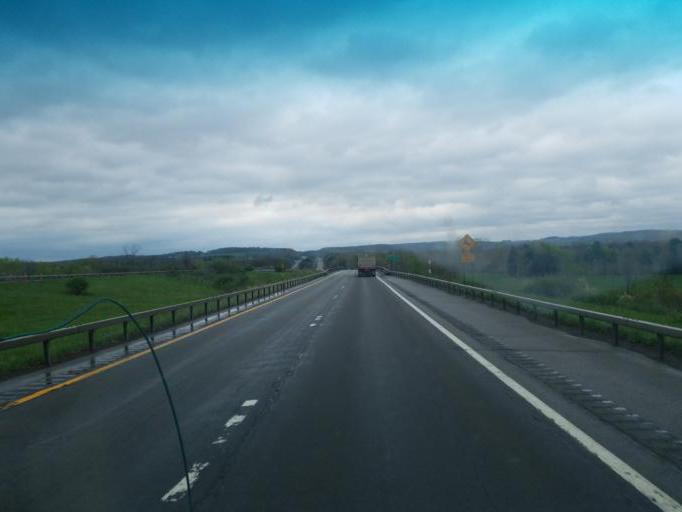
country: US
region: New York
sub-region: Chautauqua County
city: Falconer
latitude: 42.1394
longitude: -79.1120
